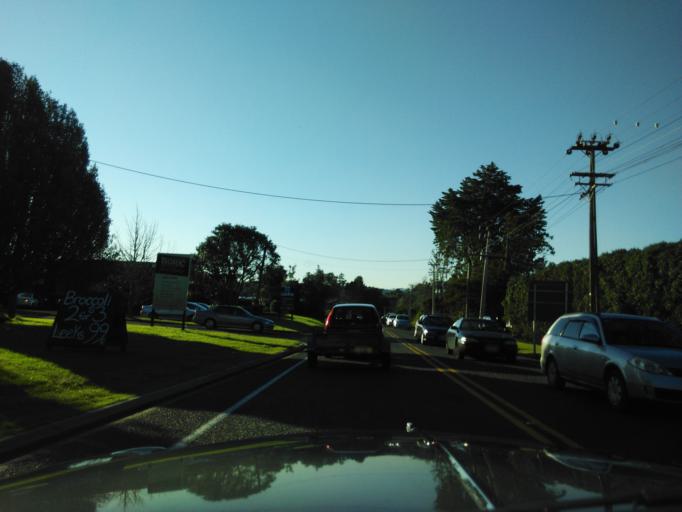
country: NZ
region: Auckland
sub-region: Auckland
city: Rosebank
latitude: -36.7877
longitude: 174.5837
